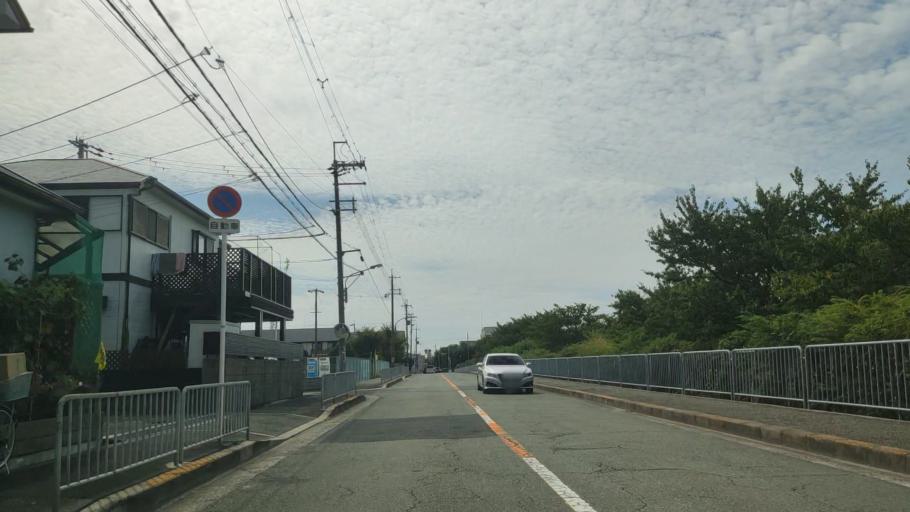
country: JP
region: Osaka
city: Ikeda
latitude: 34.8130
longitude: 135.4351
